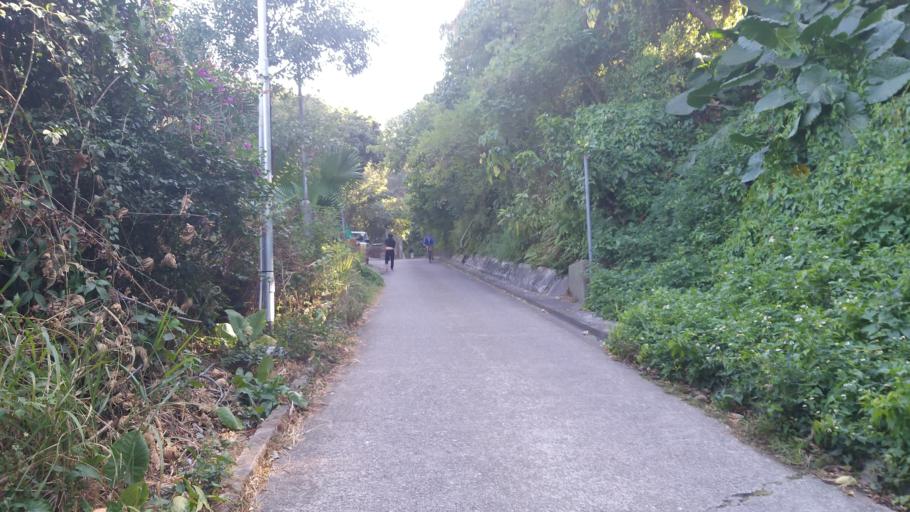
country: HK
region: Tuen Mun
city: Tuen Mun
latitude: 22.4059
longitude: 113.9858
